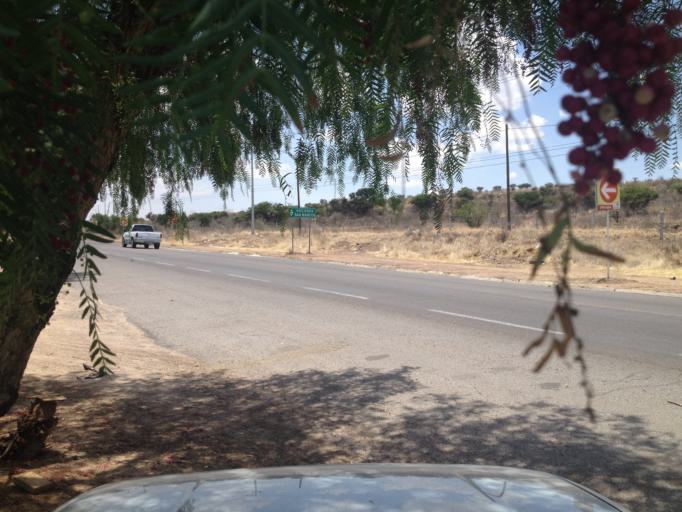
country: MX
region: Aguascalientes
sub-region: Aguascalientes
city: San Sebastian [Fraccionamiento]
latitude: 21.8057
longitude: -102.2630
